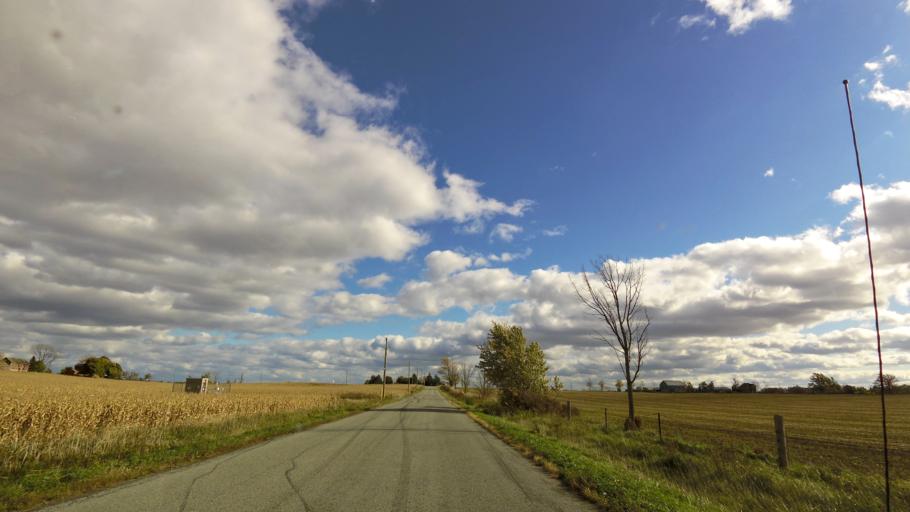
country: CA
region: Ontario
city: Burlington
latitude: 43.4349
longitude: -79.8325
